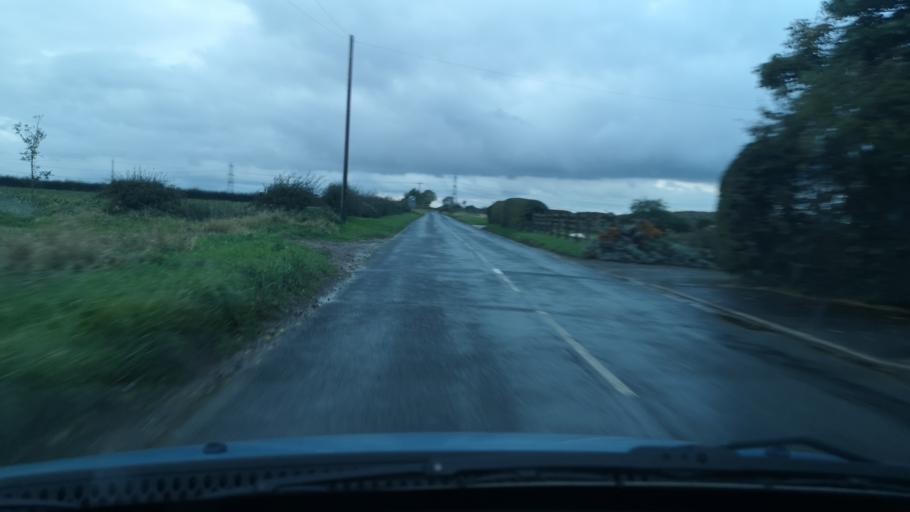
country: GB
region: England
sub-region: Doncaster
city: Norton
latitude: 53.6436
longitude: -1.2228
